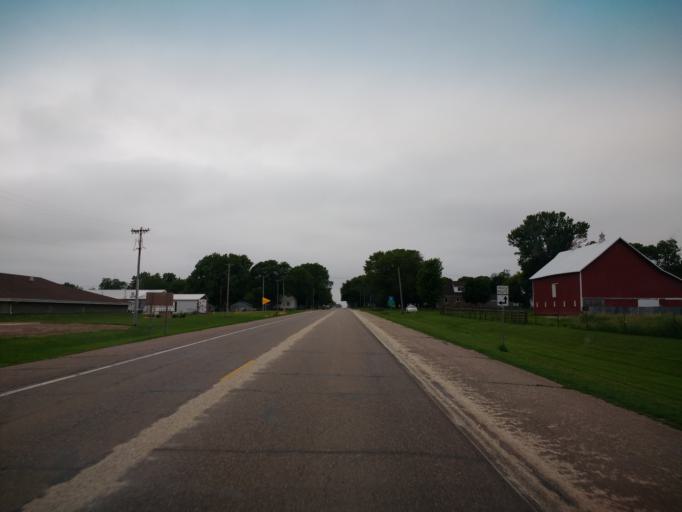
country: US
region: Iowa
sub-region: O'Brien County
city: Hartley
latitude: 43.1848
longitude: -95.4649
